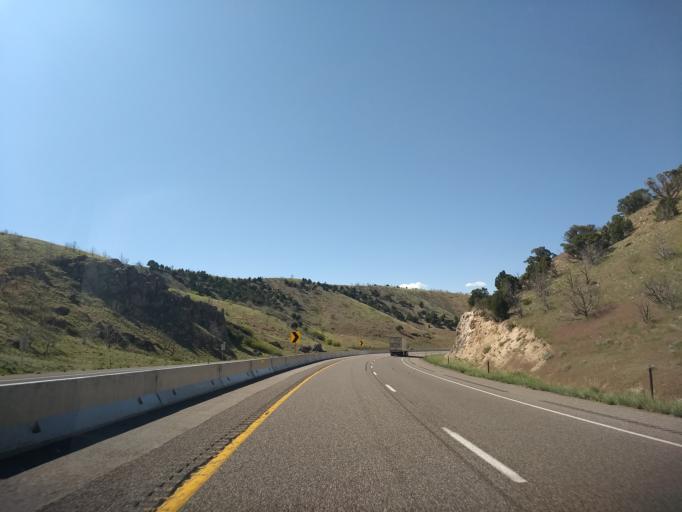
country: US
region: Utah
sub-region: Millard County
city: Fillmore
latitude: 38.6837
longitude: -112.6000
